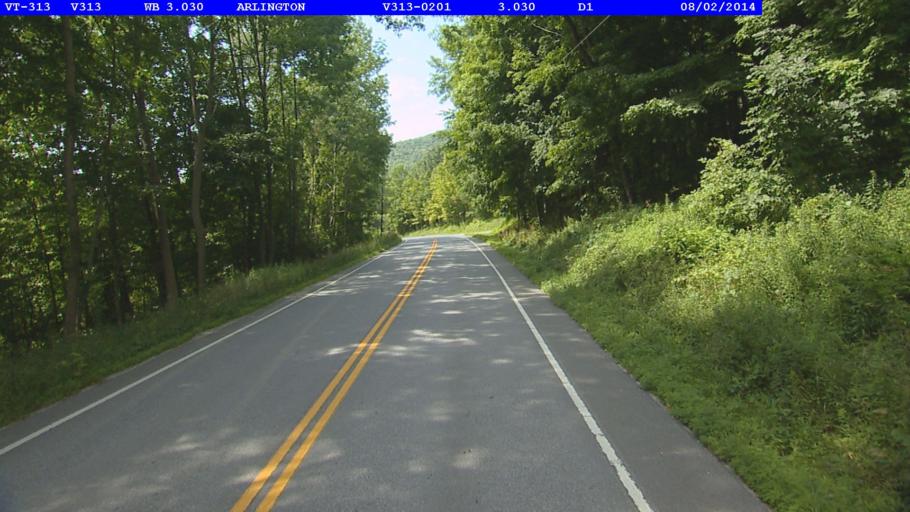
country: US
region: Vermont
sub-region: Bennington County
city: Arlington
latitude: 43.1022
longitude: -73.2090
